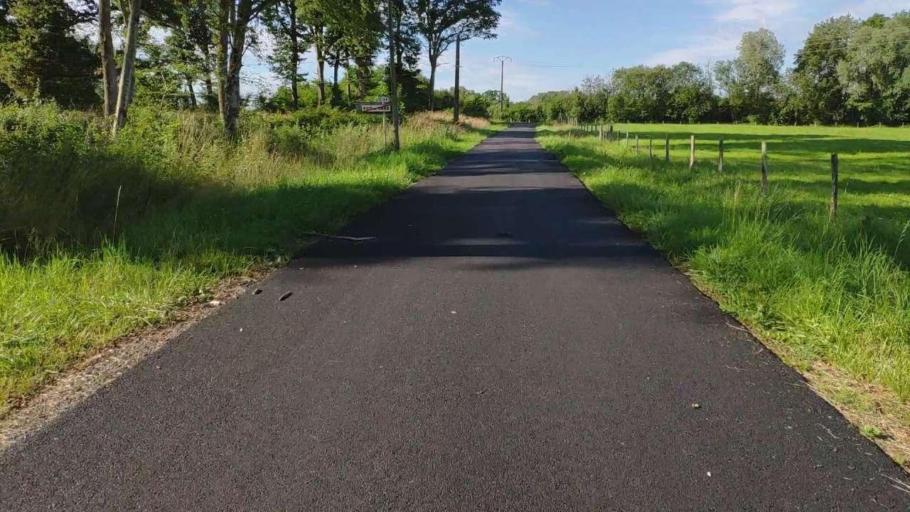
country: FR
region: Franche-Comte
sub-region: Departement du Jura
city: Bletterans
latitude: 46.8280
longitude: 5.5011
